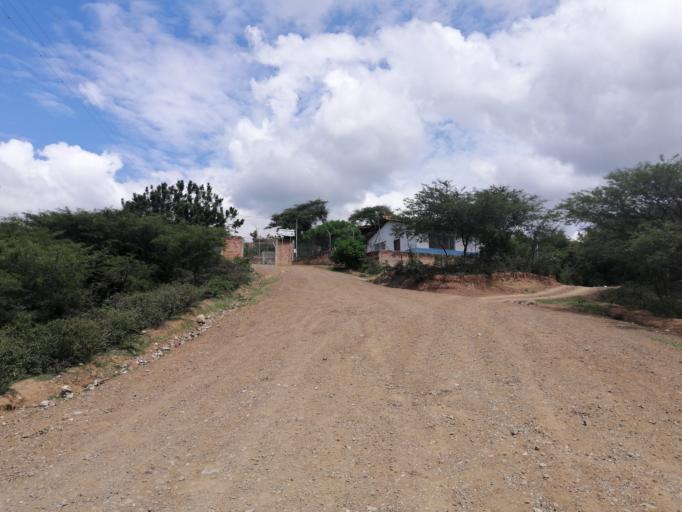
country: EC
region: Loja
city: Catacocha
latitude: -4.0126
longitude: -79.6831
